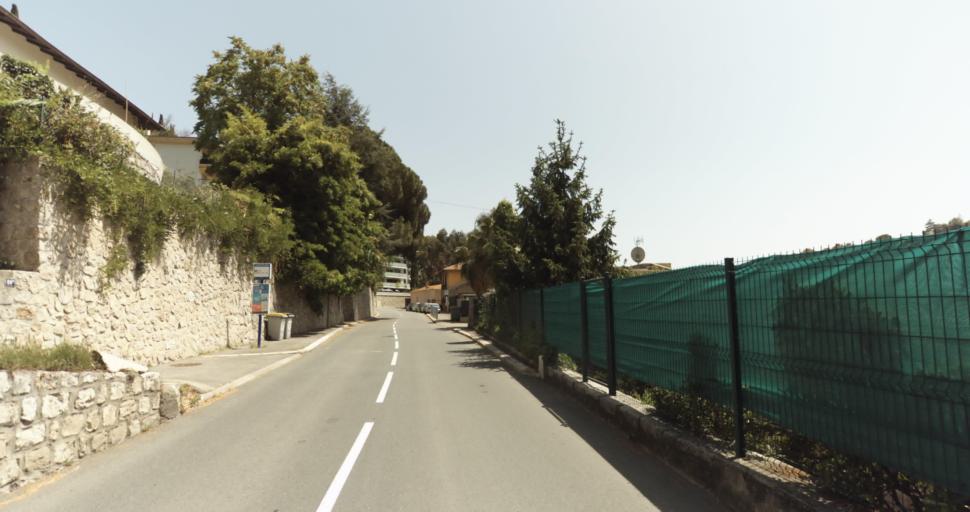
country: FR
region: Provence-Alpes-Cote d'Azur
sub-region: Departement des Alpes-Maritimes
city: Roquebrune-Cap-Martin
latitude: 43.7728
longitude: 7.4772
